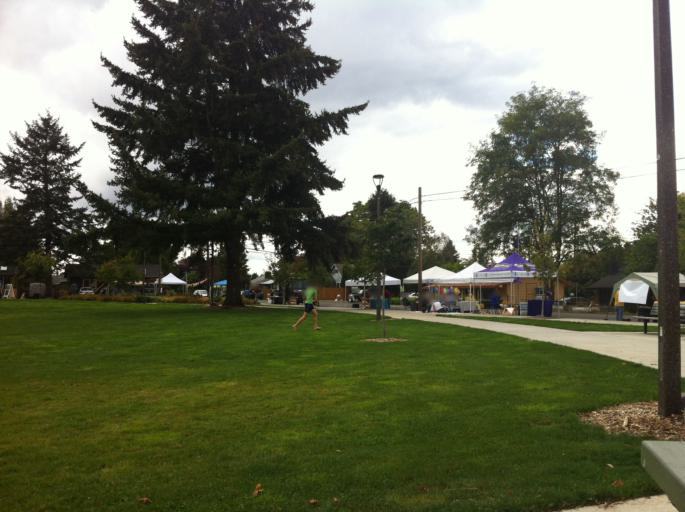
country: US
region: Oregon
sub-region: Multnomah County
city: Portland
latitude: 45.5589
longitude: -122.6086
